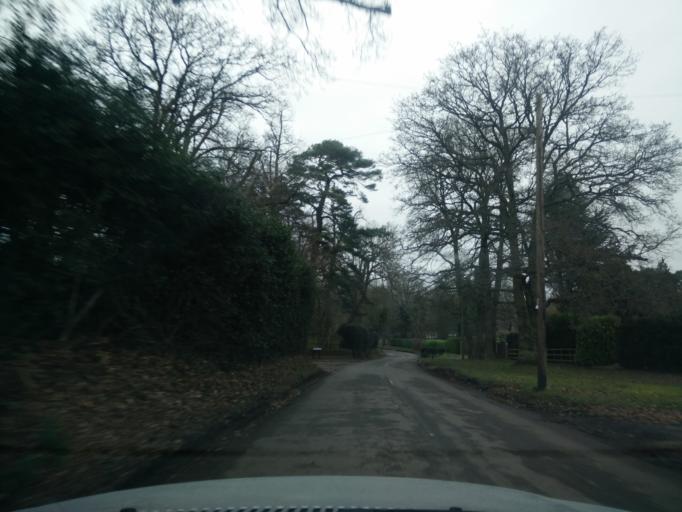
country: GB
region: England
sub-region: Buckinghamshire
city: Little Chalfont
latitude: 51.6585
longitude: -0.5569
